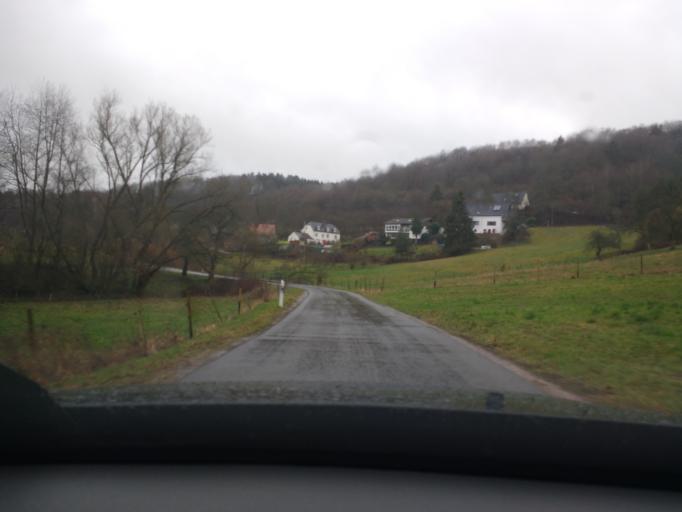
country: DE
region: Rheinland-Pfalz
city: Franzenheim
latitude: 49.6878
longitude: 6.6828
